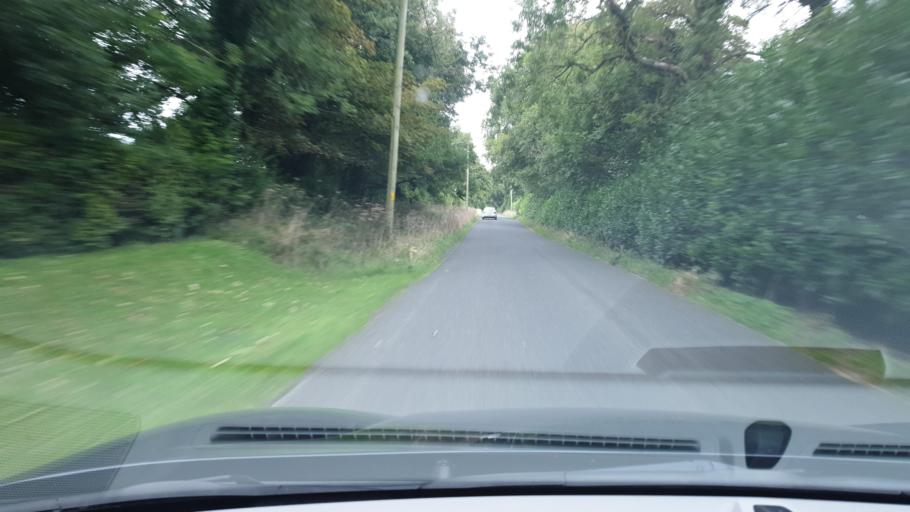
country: IE
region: Leinster
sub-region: An Mhi
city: Dunshaughlin
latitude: 53.5486
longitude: -6.5350
